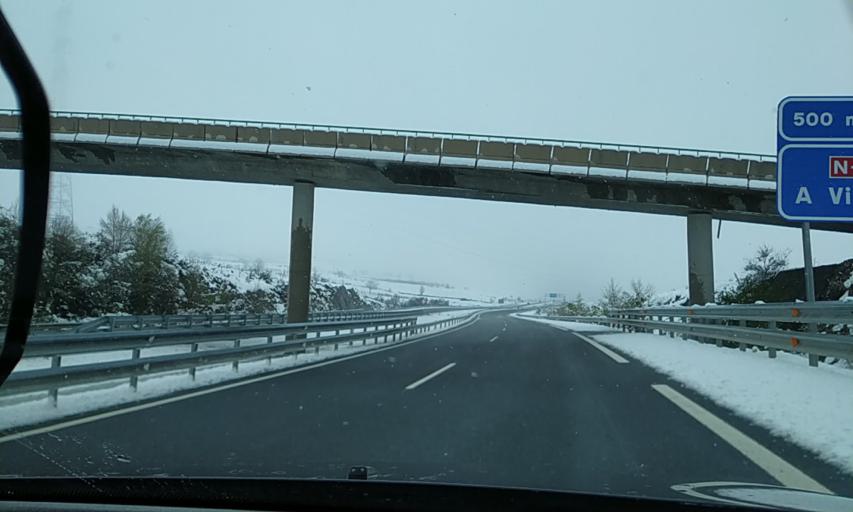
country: ES
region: Castille and Leon
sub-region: Provincia de Zamora
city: Pias
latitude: 42.0399
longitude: -7.0384
